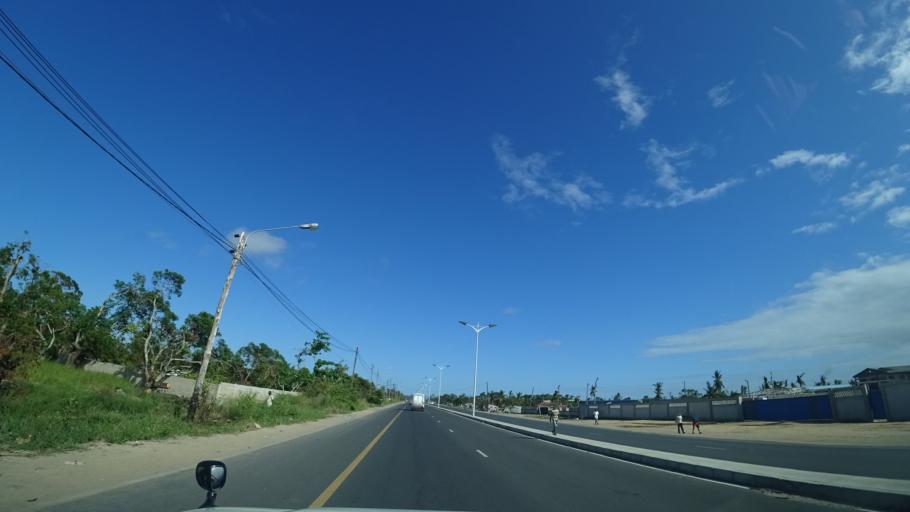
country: MZ
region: Sofala
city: Beira
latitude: -19.7368
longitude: 34.8394
